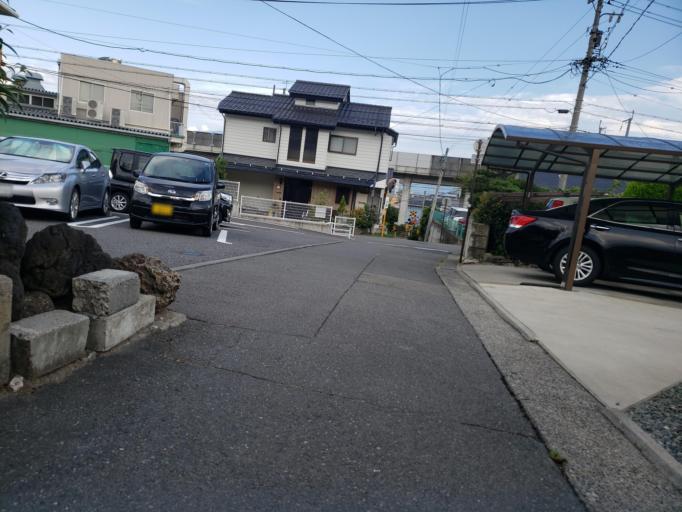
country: JP
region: Nagano
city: Nagano-shi
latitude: 36.6382
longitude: 138.1747
